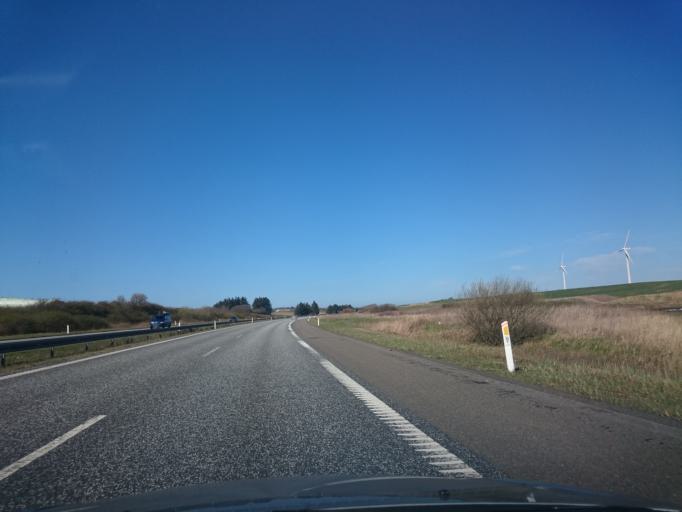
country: DK
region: North Denmark
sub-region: Hjorring Kommune
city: Hirtshals
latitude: 57.5465
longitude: 10.0063
